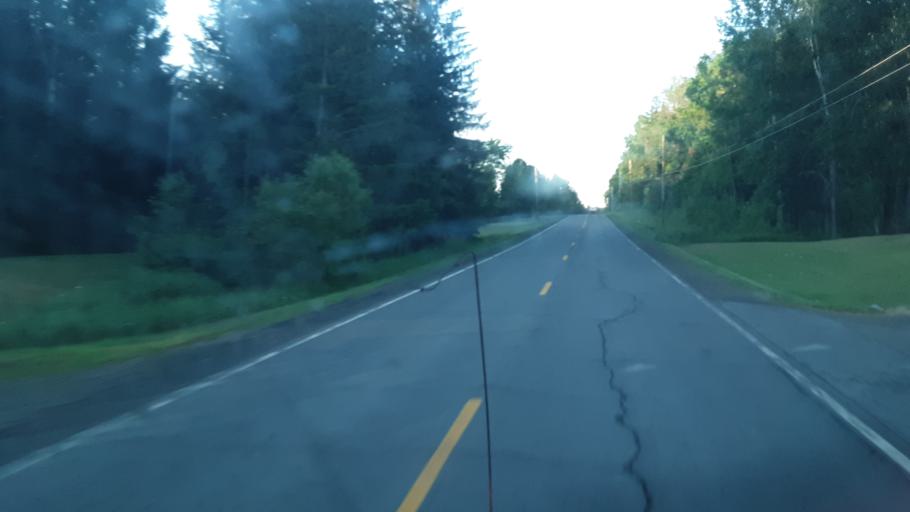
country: US
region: Maine
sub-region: Aroostook County
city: Presque Isle
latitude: 46.7356
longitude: -68.0314
